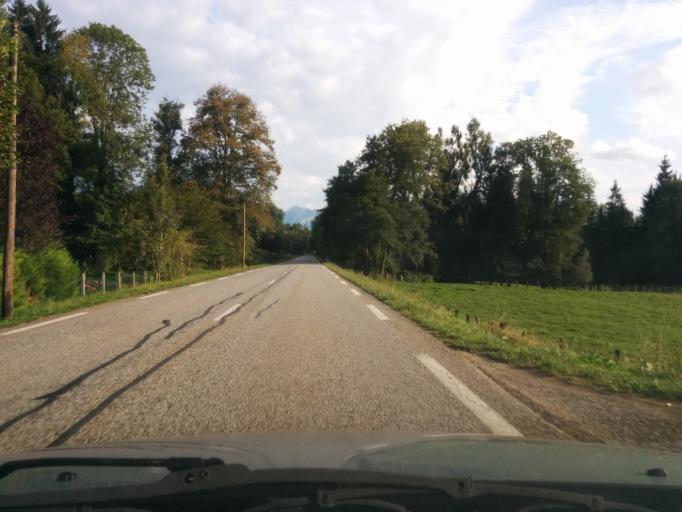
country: FR
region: Rhone-Alpes
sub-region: Departement de la Savoie
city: Les Echelles
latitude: 45.4648
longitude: 5.7367
